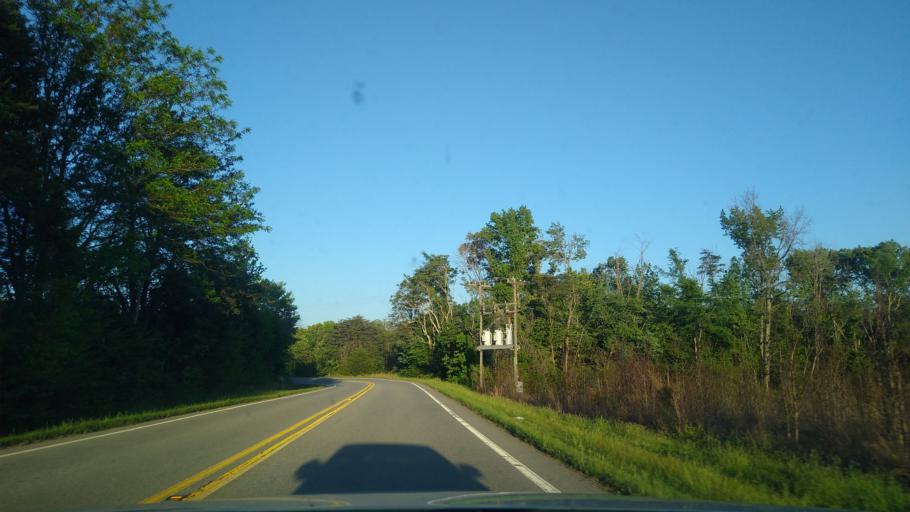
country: US
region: North Carolina
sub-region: Rockingham County
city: Reidsville
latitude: 36.3782
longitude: -79.5860
